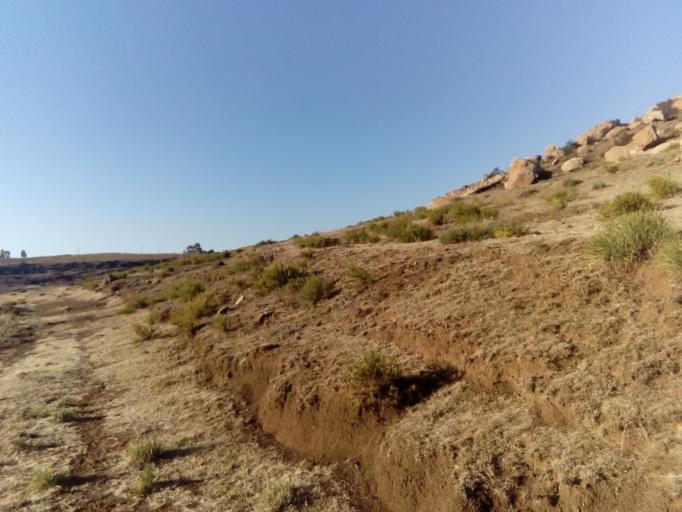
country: LS
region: Berea
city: Teyateyaneng
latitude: -29.3228
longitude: 27.8188
